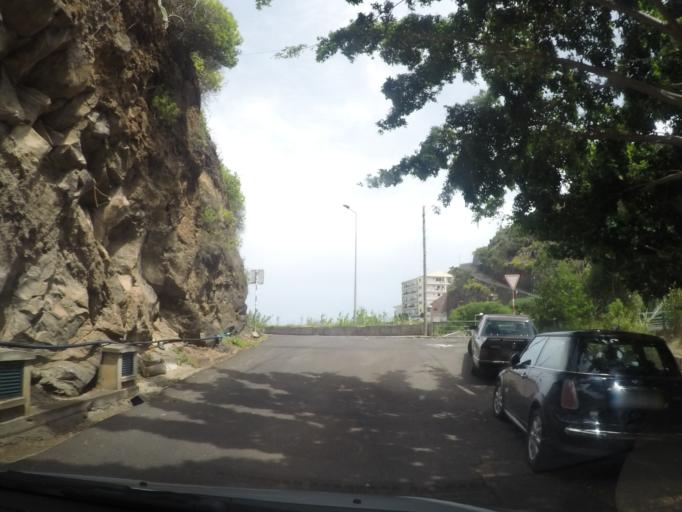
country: PT
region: Madeira
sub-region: Santa Cruz
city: Santa Cruz
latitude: 32.6846
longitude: -16.7994
